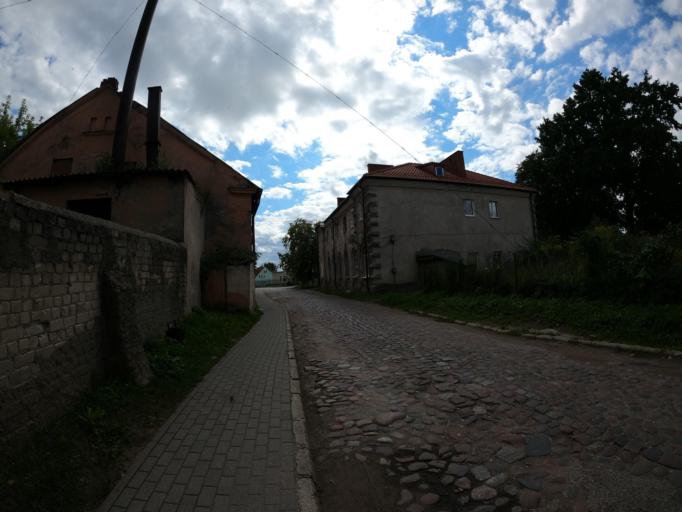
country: RU
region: Kaliningrad
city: Zheleznodorozhnyy
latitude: 54.3593
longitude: 21.3067
